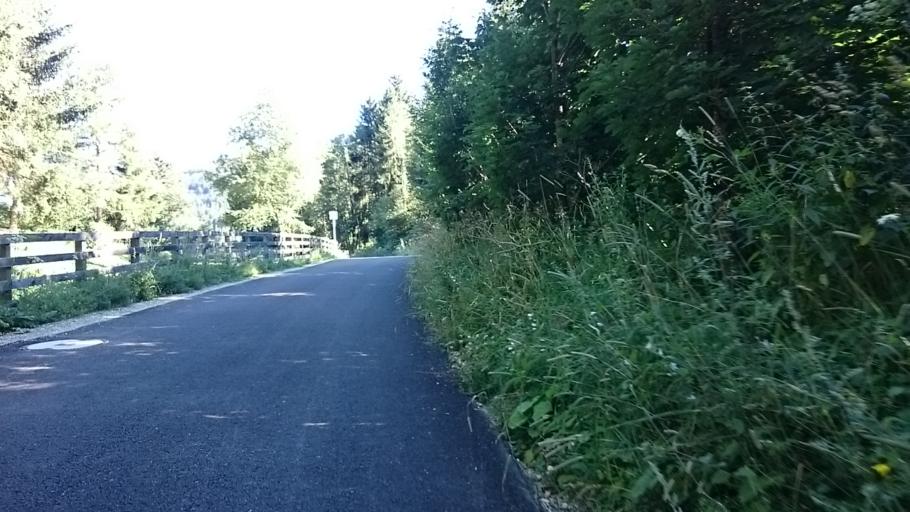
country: IT
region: Trentino-Alto Adige
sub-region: Bolzano
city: Monguelfo
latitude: 46.7466
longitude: 12.1190
